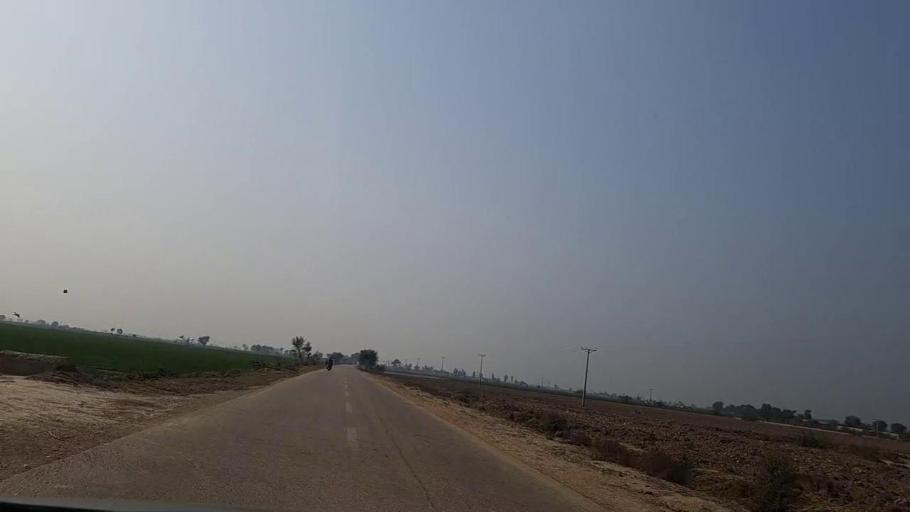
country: PK
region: Sindh
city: Sakrand
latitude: 26.1365
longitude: 68.1818
